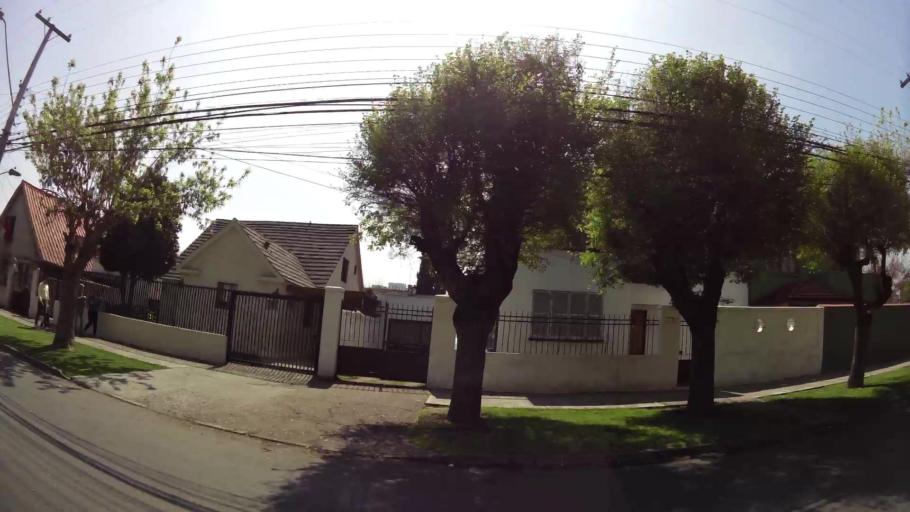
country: CL
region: Santiago Metropolitan
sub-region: Provincia de Santiago
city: Villa Presidente Frei, Nunoa, Santiago, Chile
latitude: -33.4602
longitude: -70.6105
